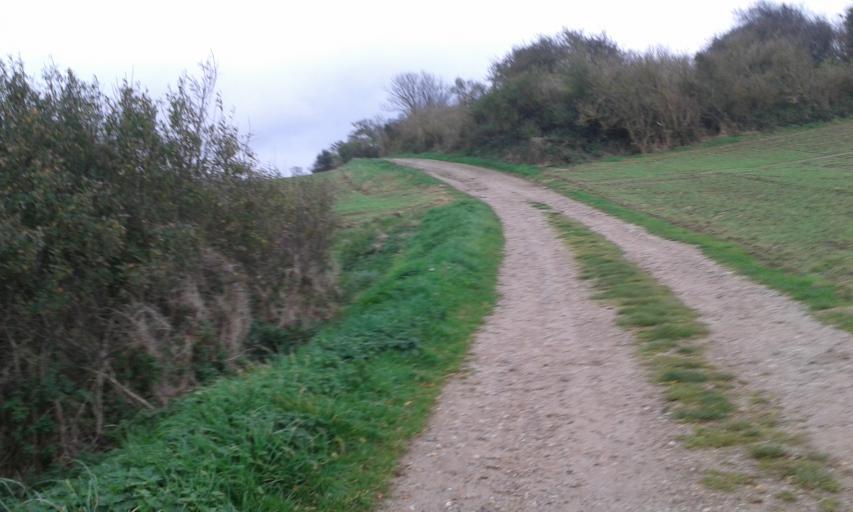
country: FR
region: Nord-Pas-de-Calais
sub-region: Departement du Pas-de-Calais
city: Wissant
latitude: 50.8849
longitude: 1.6939
